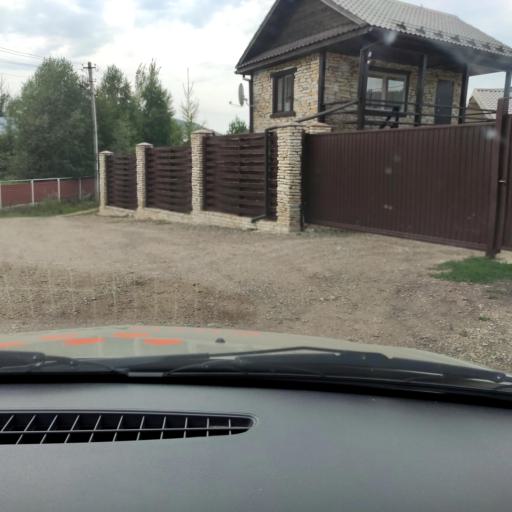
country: RU
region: Bashkortostan
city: Krasnyy Klyuch
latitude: 55.3795
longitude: 56.6738
